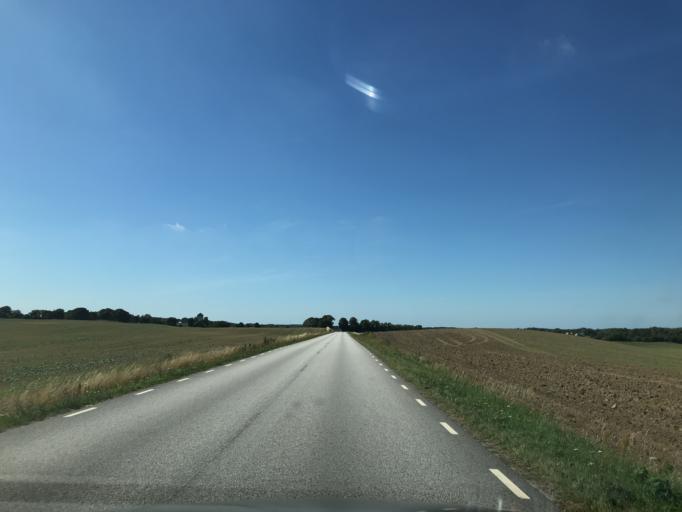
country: SE
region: Skane
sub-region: Tomelilla Kommun
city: Tomelilla
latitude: 55.6431
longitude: 13.9944
